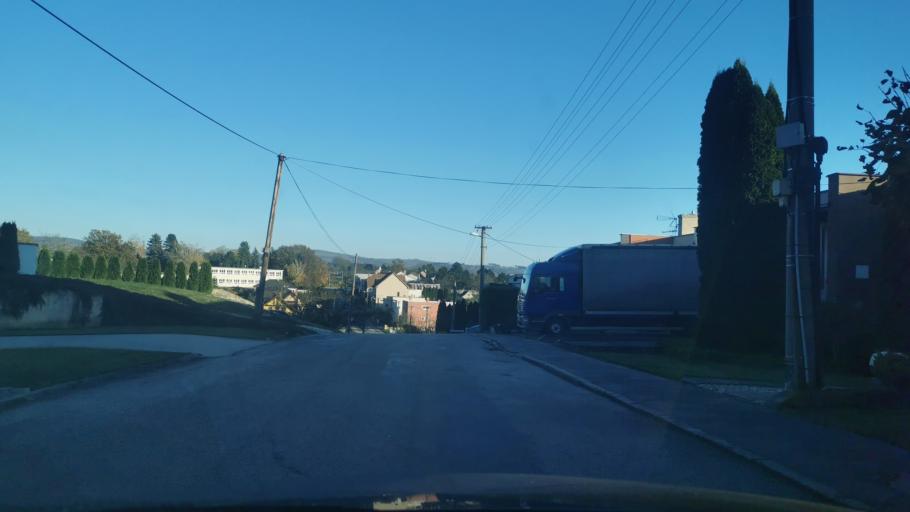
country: SK
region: Trnavsky
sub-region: Okres Skalica
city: Skalica
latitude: 48.7748
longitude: 17.2753
